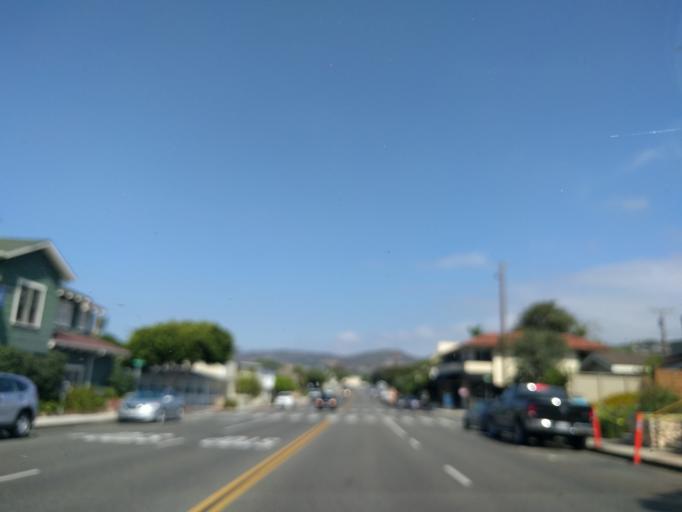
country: US
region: California
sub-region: Orange County
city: Laguna Beach
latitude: 33.5334
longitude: -117.7753
